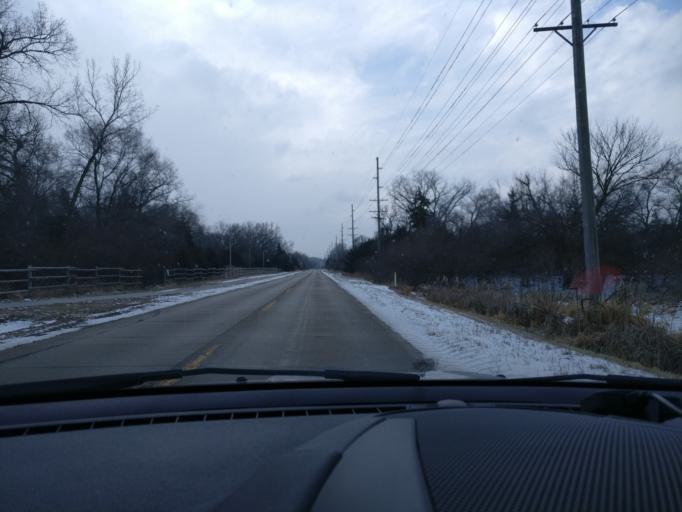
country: US
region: Nebraska
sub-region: Dodge County
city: Fremont
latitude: 41.4281
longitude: -96.5215
